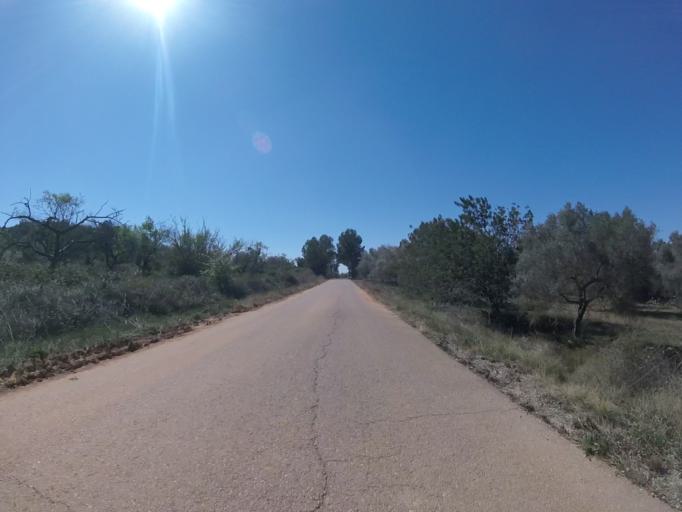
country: ES
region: Valencia
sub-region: Provincia de Castello
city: Cuevas de Vinroma
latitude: 40.3953
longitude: 0.1632
